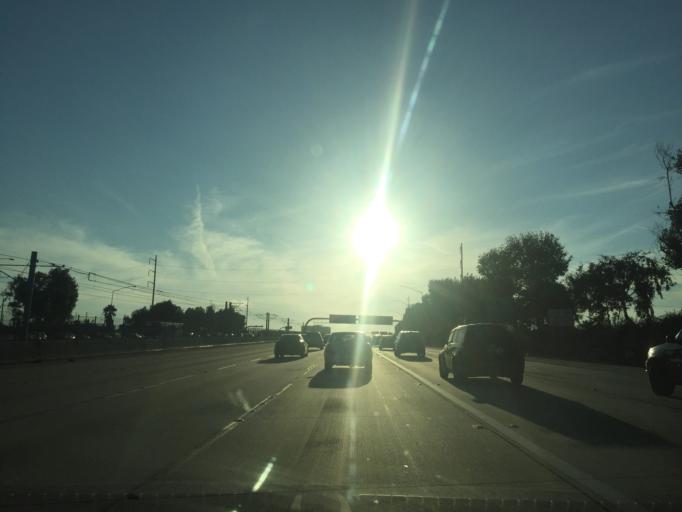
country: US
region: California
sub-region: Los Angeles County
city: Lennox
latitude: 33.9335
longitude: -118.3570
